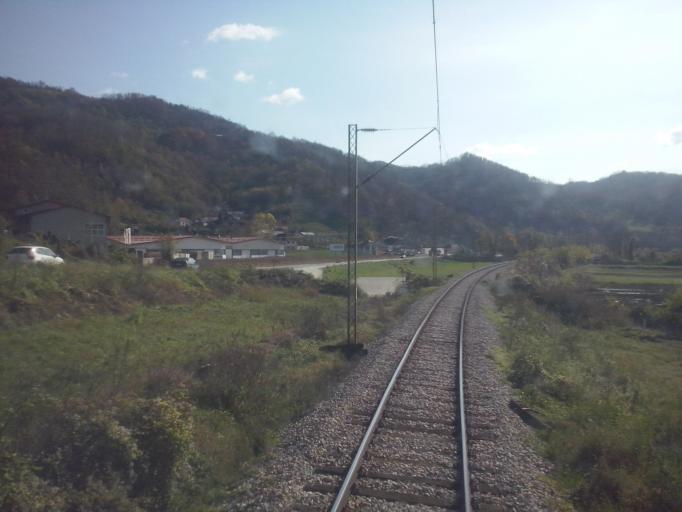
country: RS
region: Central Serbia
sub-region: Zlatiborski Okrug
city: Pozega
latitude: 43.9110
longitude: 19.9999
